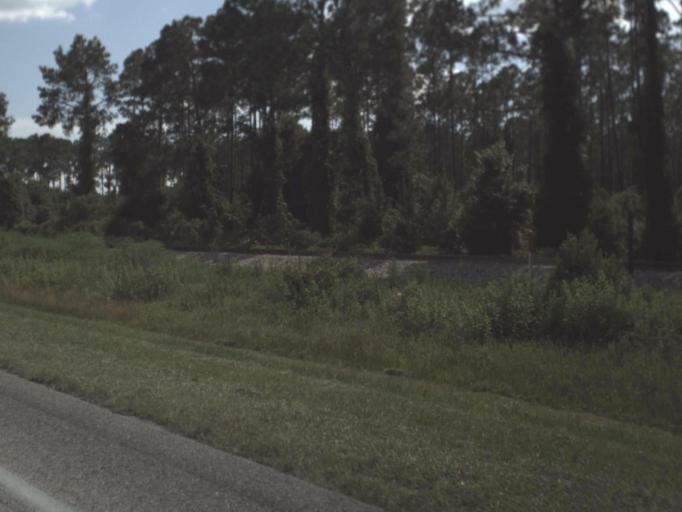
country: US
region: Florida
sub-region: Alachua County
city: Hawthorne
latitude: 29.5372
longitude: -82.1009
